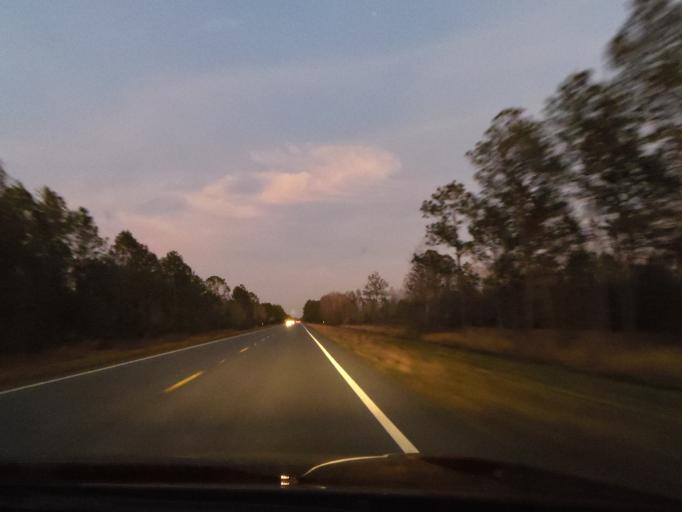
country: US
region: Florida
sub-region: Volusia County
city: De Leon Springs
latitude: 29.2321
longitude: -81.2844
